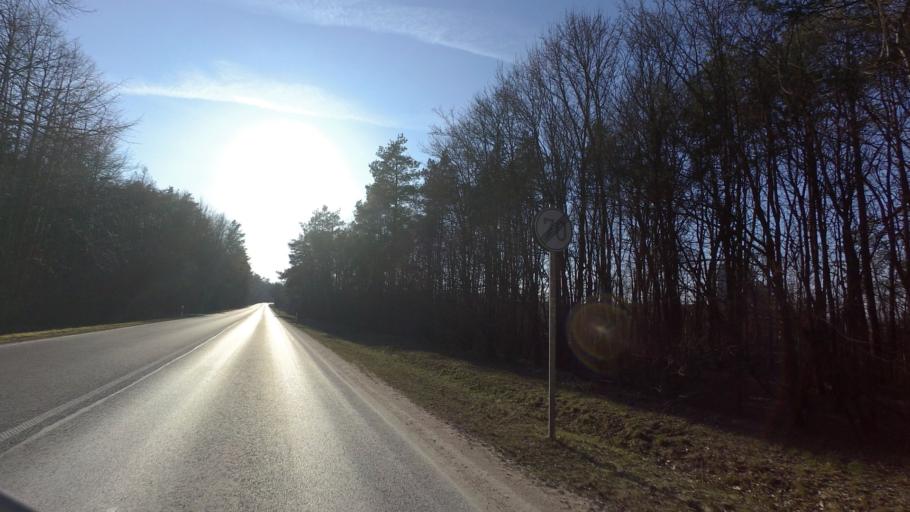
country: DE
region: Brandenburg
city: Althuttendorf
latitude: 52.9523
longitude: 13.8485
